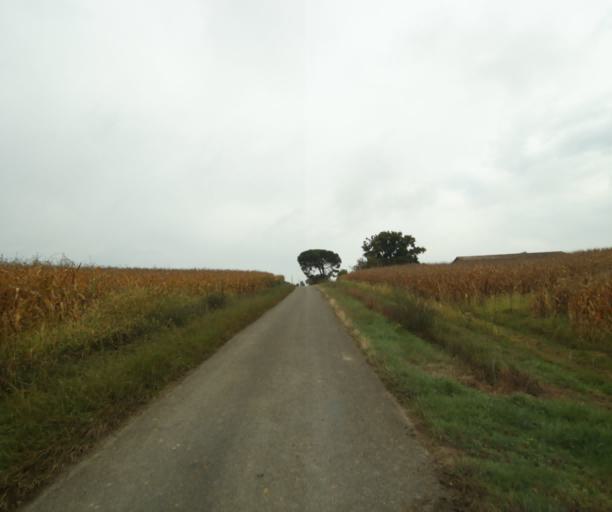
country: FR
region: Midi-Pyrenees
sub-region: Departement du Gers
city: Cazaubon
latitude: 43.9253
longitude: -0.1581
